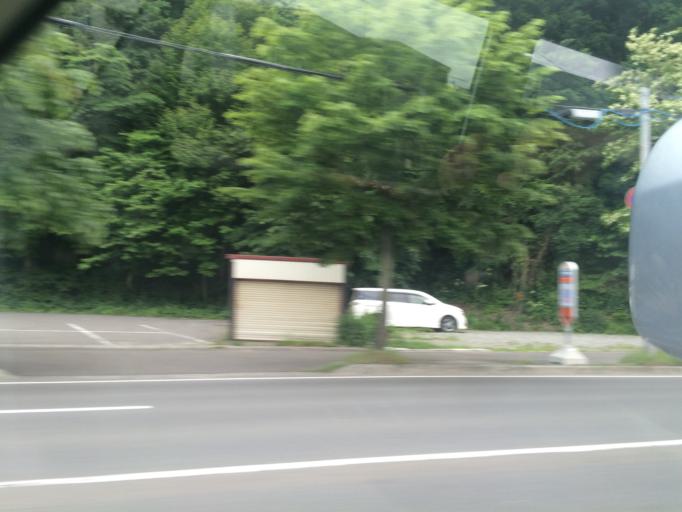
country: JP
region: Hokkaido
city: Sapporo
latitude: 43.0198
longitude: 141.3442
